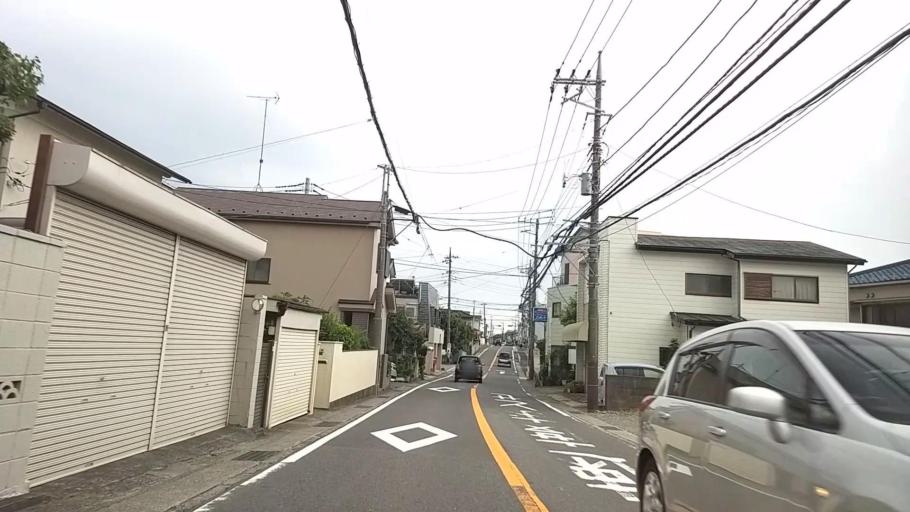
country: JP
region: Kanagawa
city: Minami-rinkan
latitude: 35.4633
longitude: 139.4237
